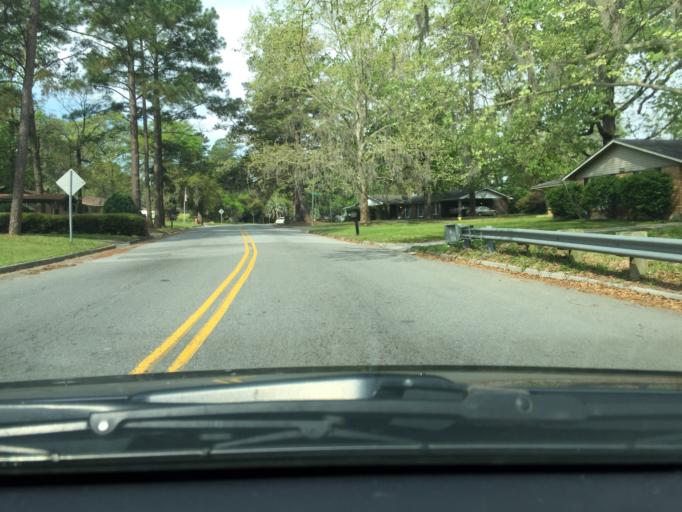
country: US
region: Georgia
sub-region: Chatham County
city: Montgomery
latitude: 31.9850
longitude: -81.1371
